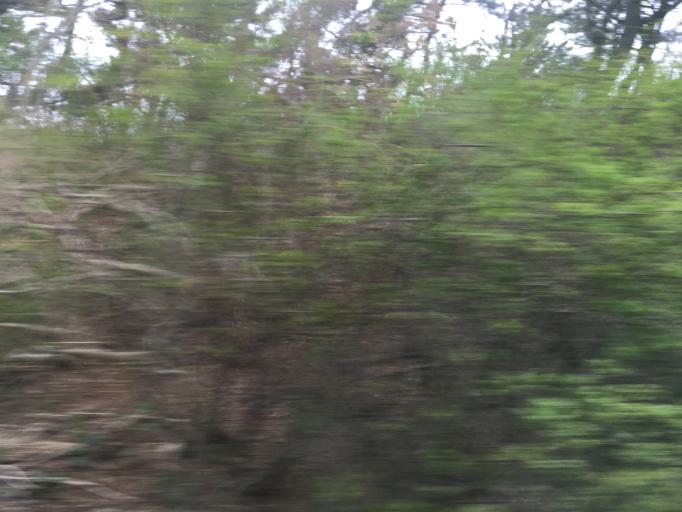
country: JP
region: Aomori
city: Shimokizukuri
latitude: 40.7658
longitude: 140.1663
